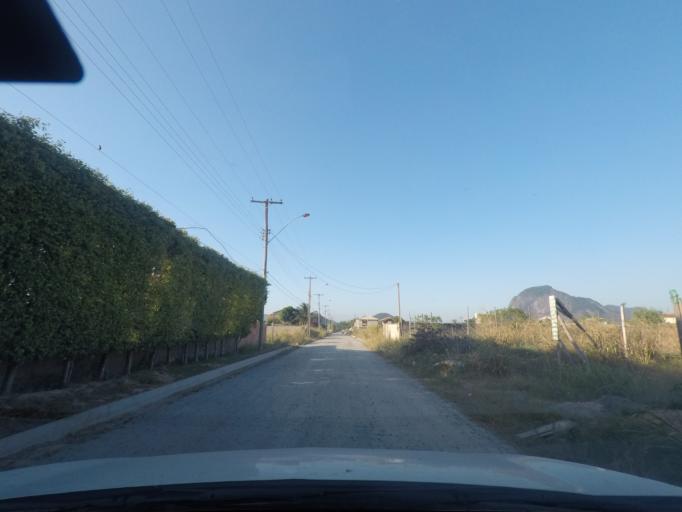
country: BR
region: Rio de Janeiro
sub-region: Marica
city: Marica
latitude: -22.9611
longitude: -42.9334
